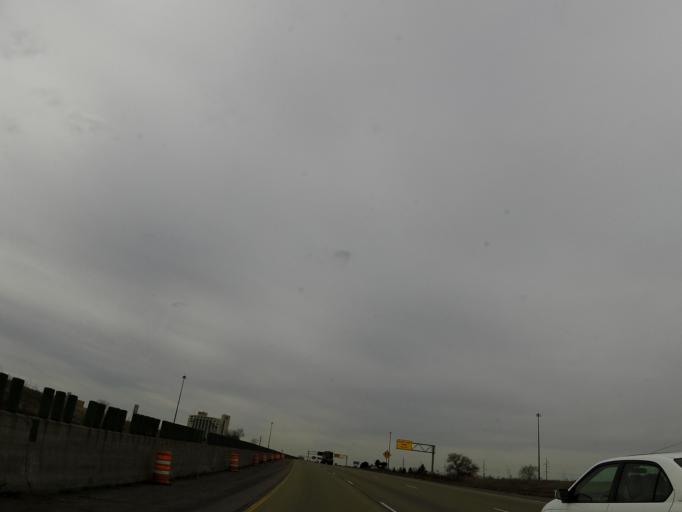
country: US
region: Minnesota
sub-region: Dakota County
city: Eagan
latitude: 44.8630
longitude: -93.2106
